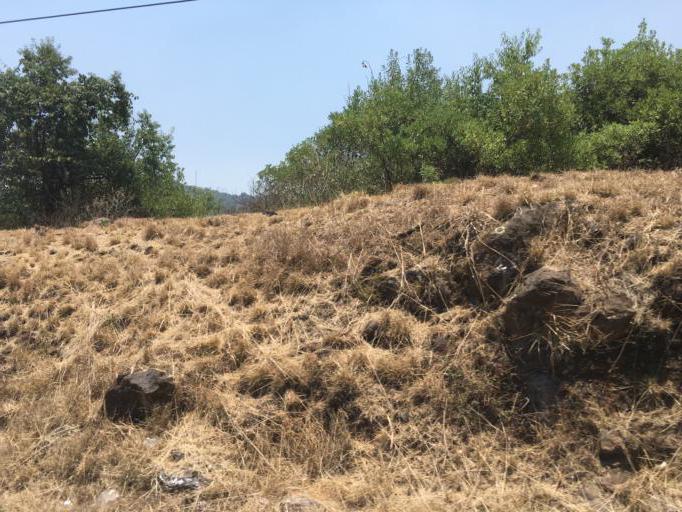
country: MX
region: Michoacan
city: Quiroga
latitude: 19.6623
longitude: -101.5133
